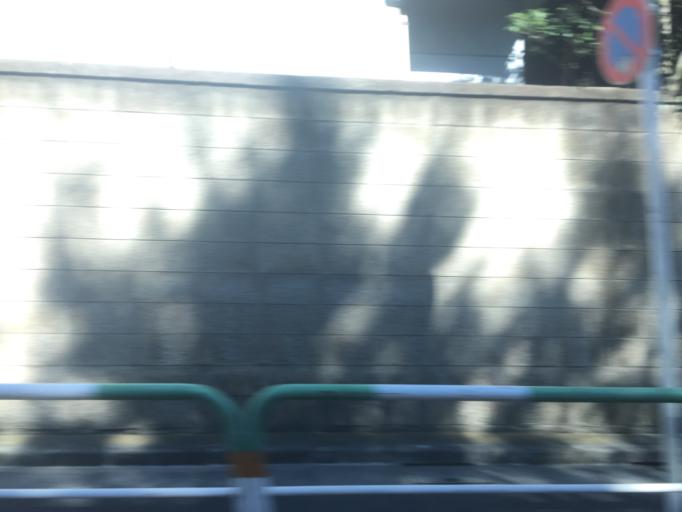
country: JP
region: Tokyo
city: Tokyo
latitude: 35.6508
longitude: 139.6993
